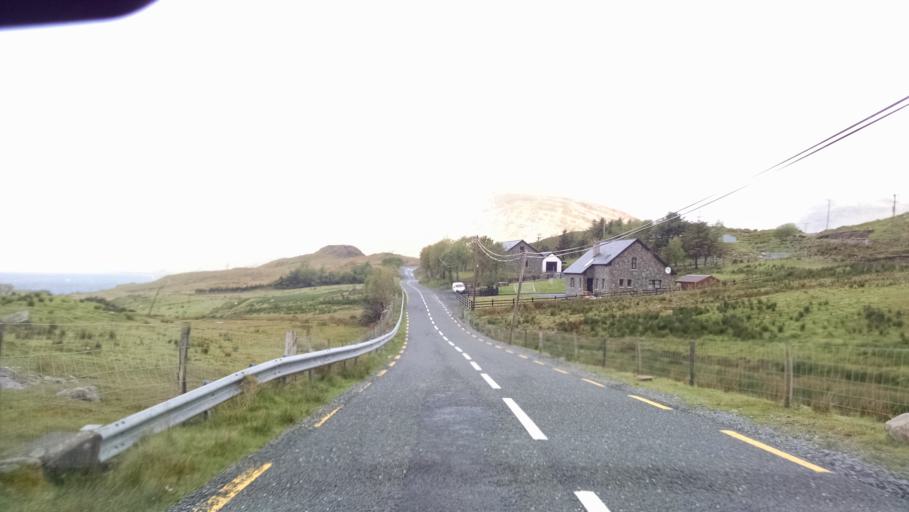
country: IE
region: Connaught
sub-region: Maigh Eo
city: Westport
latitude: 53.6041
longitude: -9.7376
